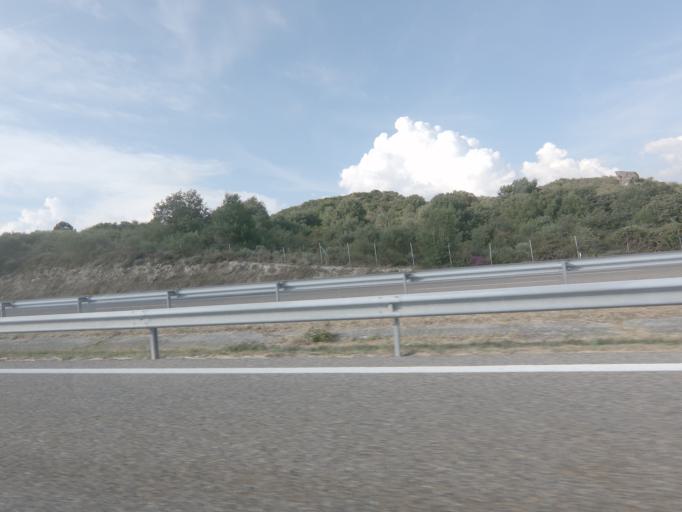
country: ES
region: Galicia
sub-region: Provincia de Ourense
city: Cualedro
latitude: 41.9900
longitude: -7.5557
